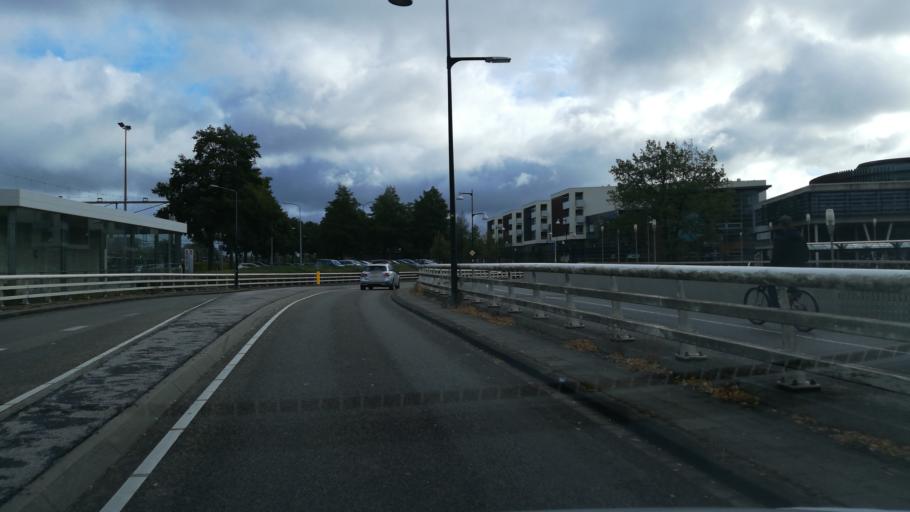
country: NL
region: Gelderland
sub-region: Gemeente Apeldoorn
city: Apeldoorn
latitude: 52.2090
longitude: 5.9687
